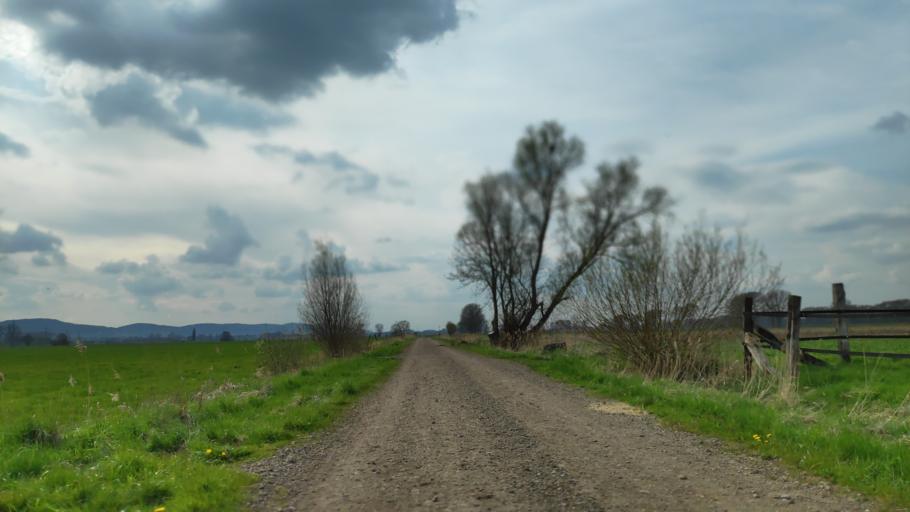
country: DE
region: North Rhine-Westphalia
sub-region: Regierungsbezirk Detmold
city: Minden
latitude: 52.2873
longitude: 8.8584
